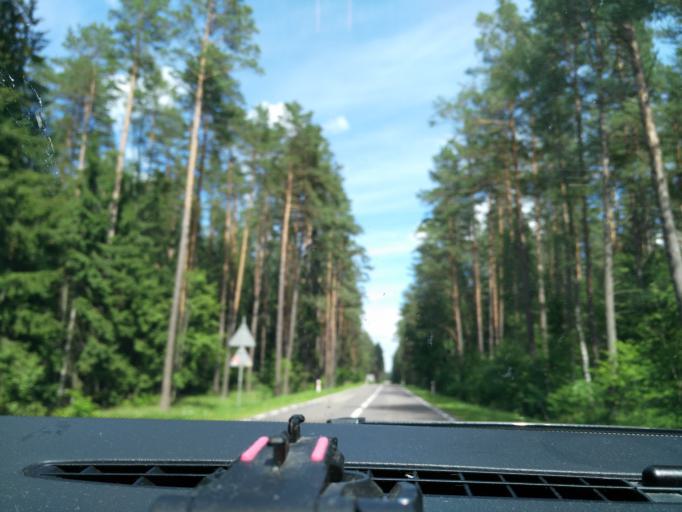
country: PL
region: Podlasie
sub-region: Powiat sejnenski
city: Krasnopol
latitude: 53.9661
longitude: 23.2426
